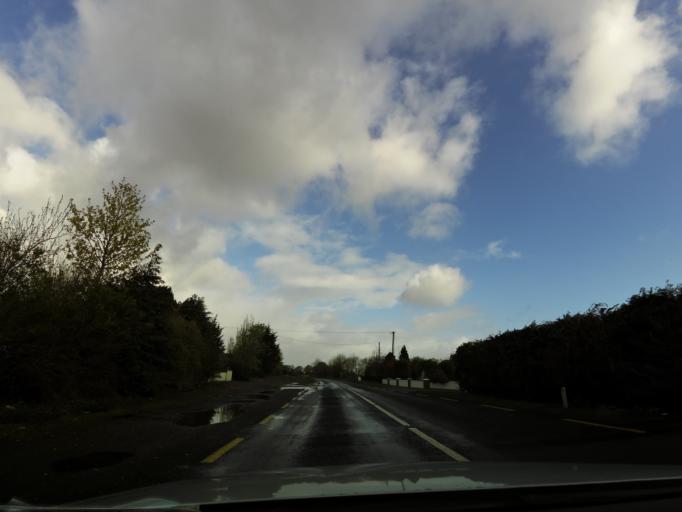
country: IE
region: Munster
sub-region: North Tipperary
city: Nenagh
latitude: 52.8400
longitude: -8.1367
